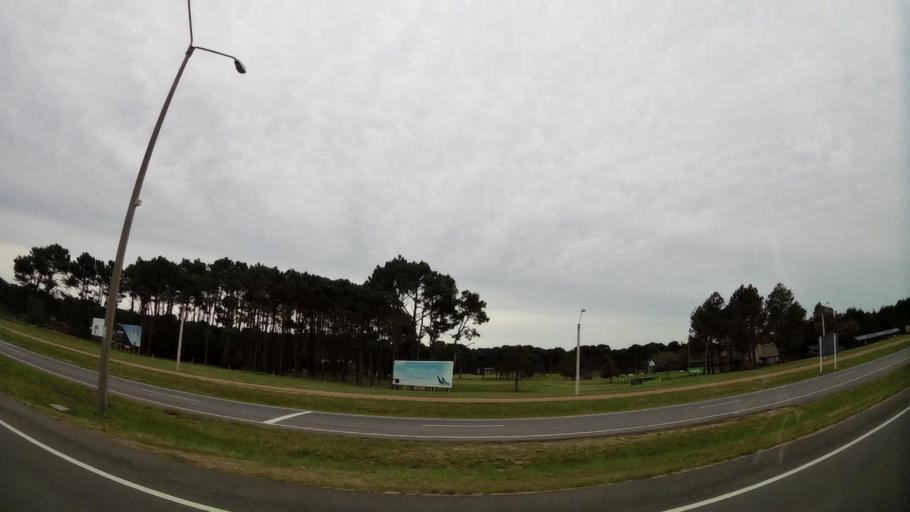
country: UY
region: Maldonado
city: Maldonado
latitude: -34.8746
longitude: -55.0670
